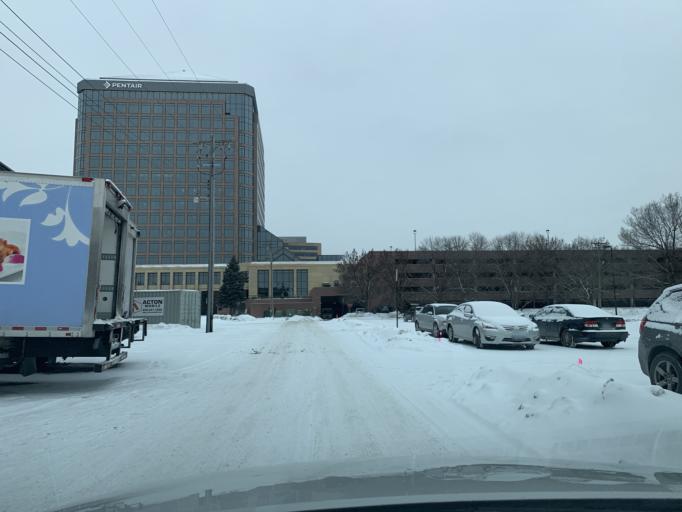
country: US
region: Minnesota
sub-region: Hennepin County
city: Saint Louis Park
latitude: 44.9717
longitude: -93.3482
